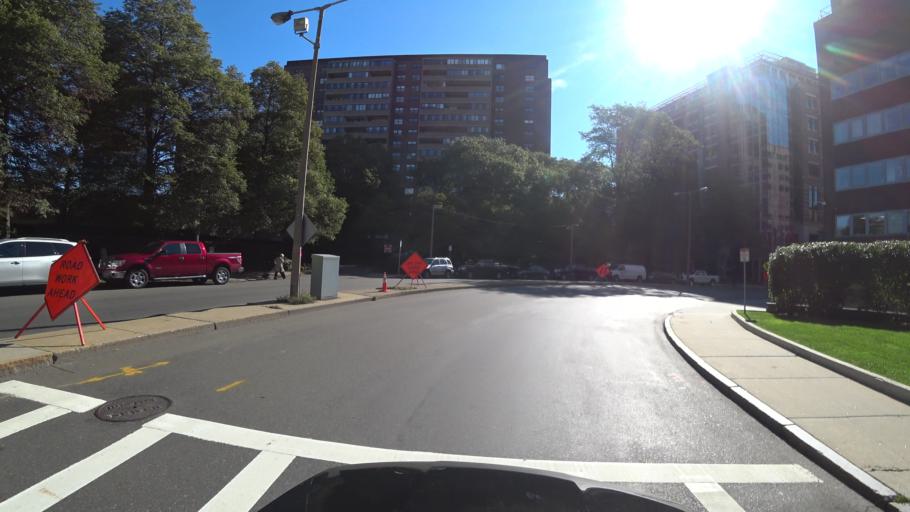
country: US
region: Massachusetts
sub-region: Suffolk County
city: Boston
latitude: 42.3639
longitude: -71.0674
